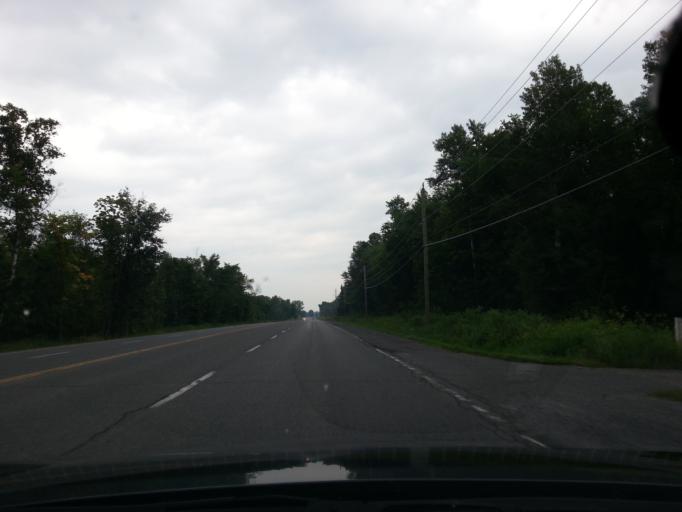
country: CA
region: Quebec
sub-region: Outaouais
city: Thurso
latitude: 45.5669
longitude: -75.2160
